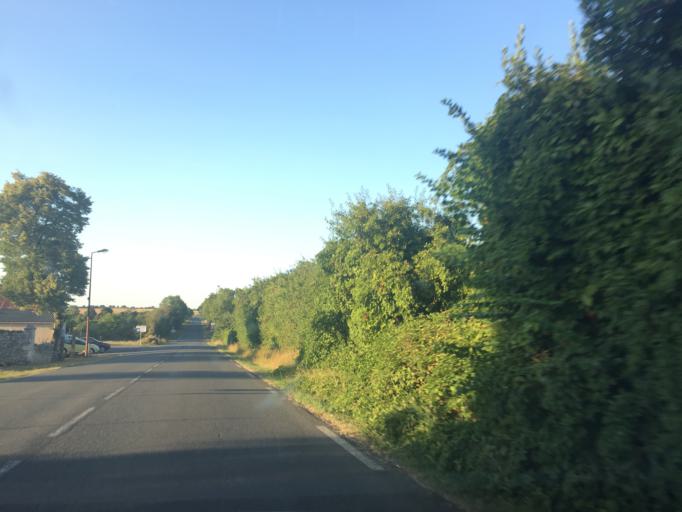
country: FR
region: Poitou-Charentes
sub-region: Departement des Deux-Sevres
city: Lezay
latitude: 46.3263
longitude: -0.0332
